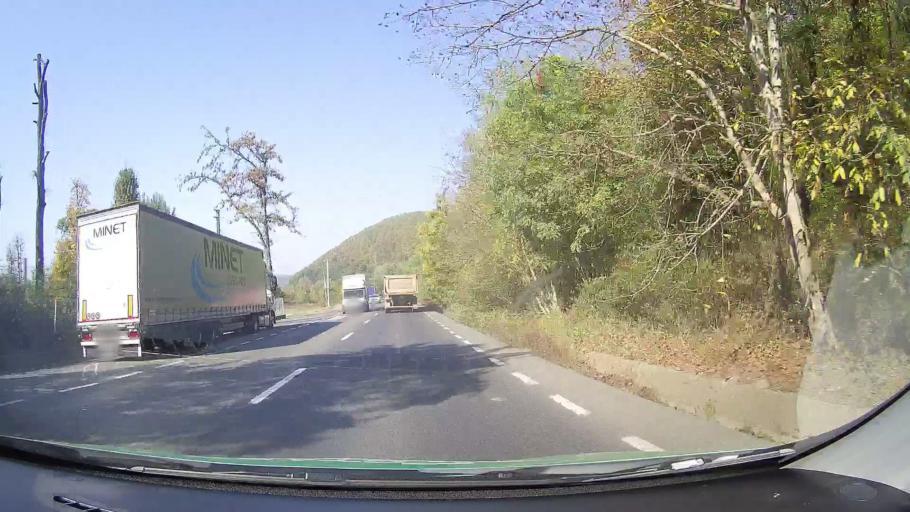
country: RO
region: Hunedoara
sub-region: Comuna Zam
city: Zam
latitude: 46.0099
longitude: 22.4411
